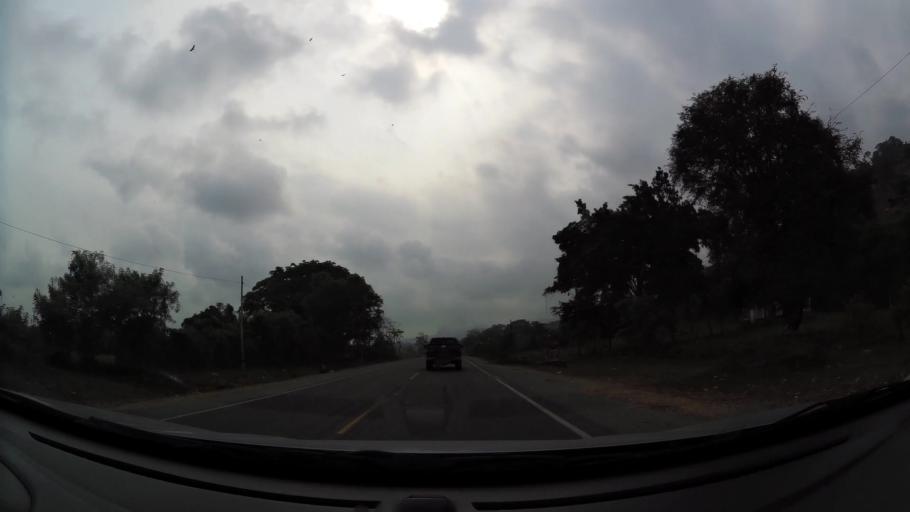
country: HN
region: Yoro
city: Guaimitas
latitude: 15.4935
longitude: -87.7417
